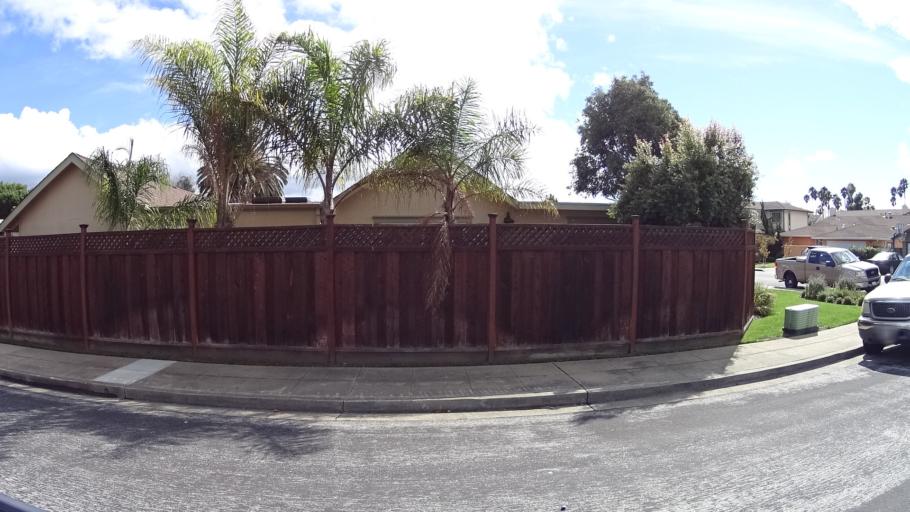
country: US
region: California
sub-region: San Mateo County
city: Foster City
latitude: 37.5599
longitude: -122.2612
